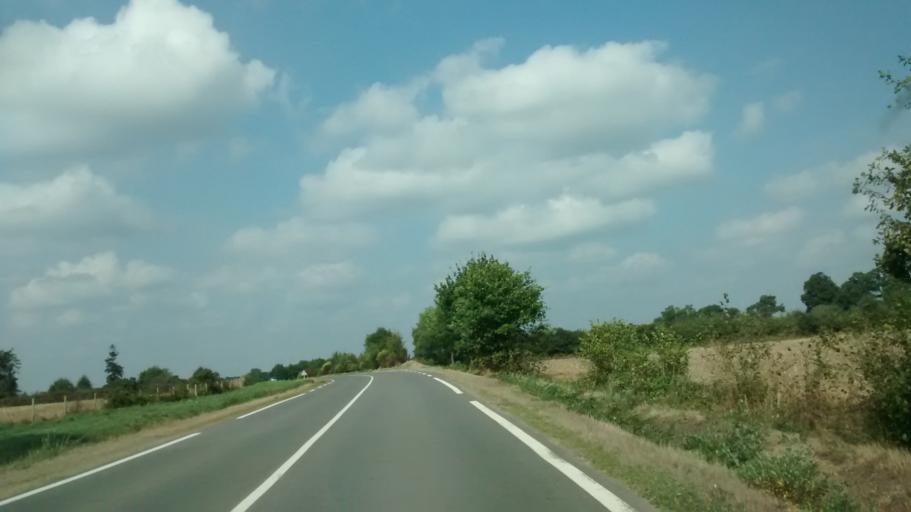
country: FR
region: Brittany
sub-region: Departement d'Ille-et-Vilaine
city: Livre-sur-Changeon
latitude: 48.2375
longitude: -1.3595
